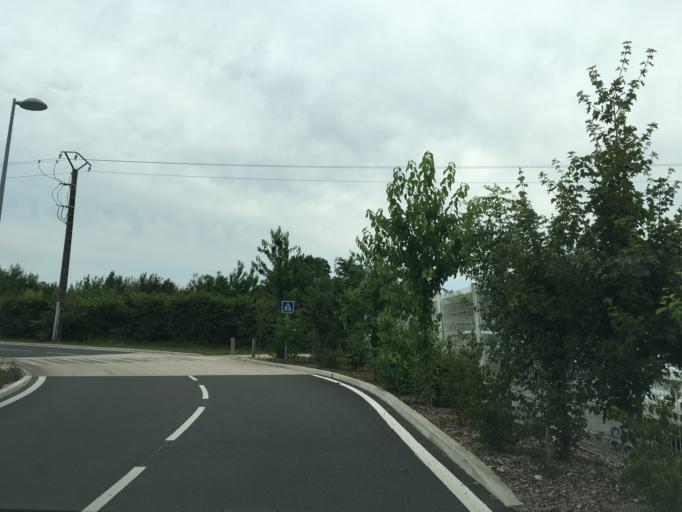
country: FR
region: Poitou-Charentes
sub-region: Departement des Deux-Sevres
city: Bessines
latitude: 46.3057
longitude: -0.4850
